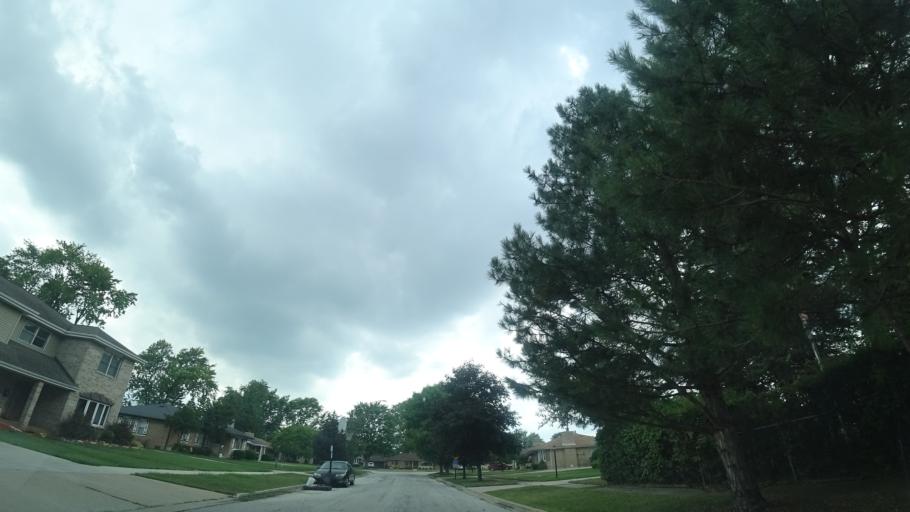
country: US
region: Illinois
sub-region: Cook County
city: Chicago Ridge
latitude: 41.6934
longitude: -87.7669
